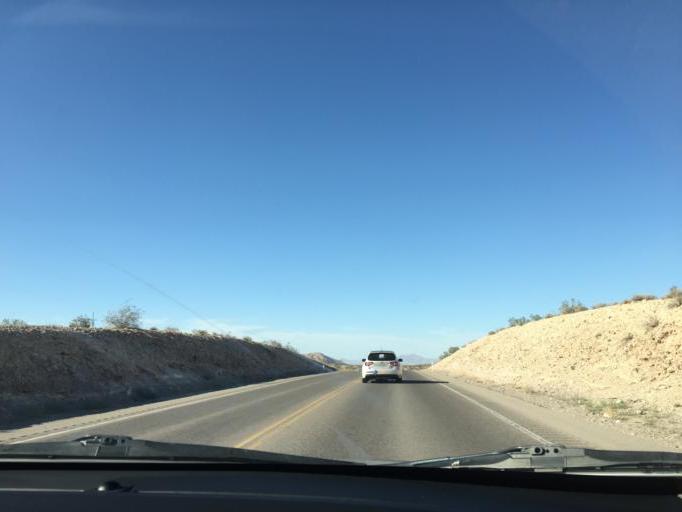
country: US
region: Nevada
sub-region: Clark County
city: Enterprise
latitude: 35.8803
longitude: -115.2279
